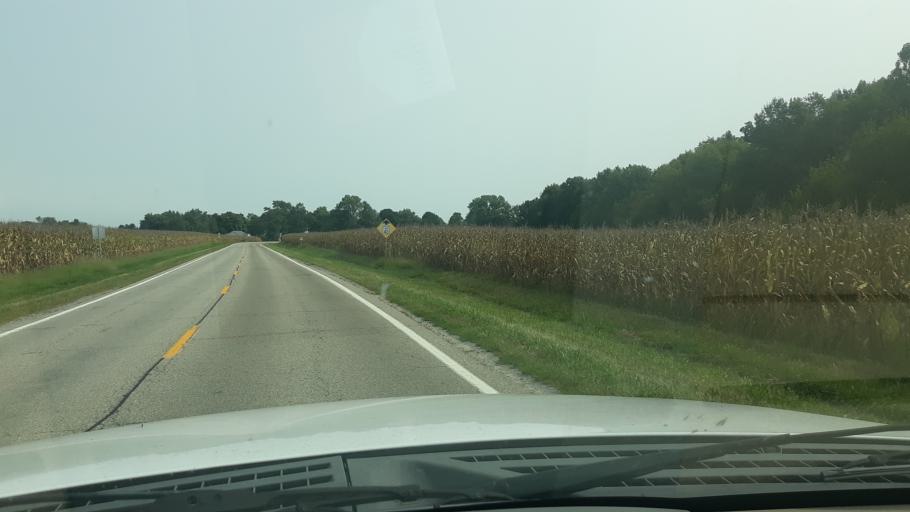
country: US
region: Illinois
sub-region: Edwards County
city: Grayville
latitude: 38.3072
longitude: -87.9435
